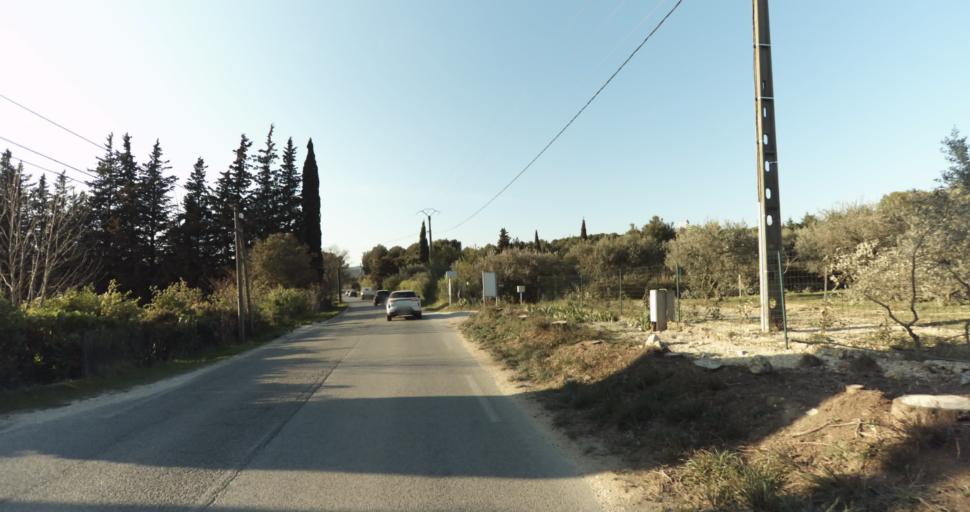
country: FR
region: Provence-Alpes-Cote d'Azur
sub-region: Departement des Bouches-du-Rhone
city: Ventabren
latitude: 43.5292
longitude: 5.2851
